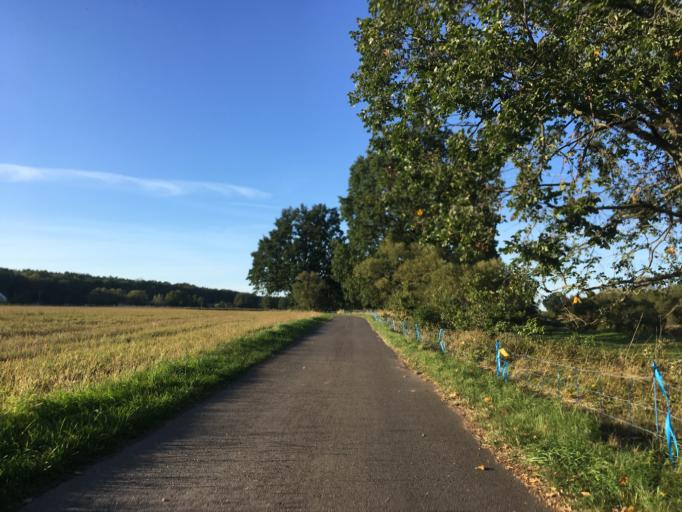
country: PL
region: Lubusz
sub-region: Powiat zarski
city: Trzebiel
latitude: 51.6349
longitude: 14.7541
